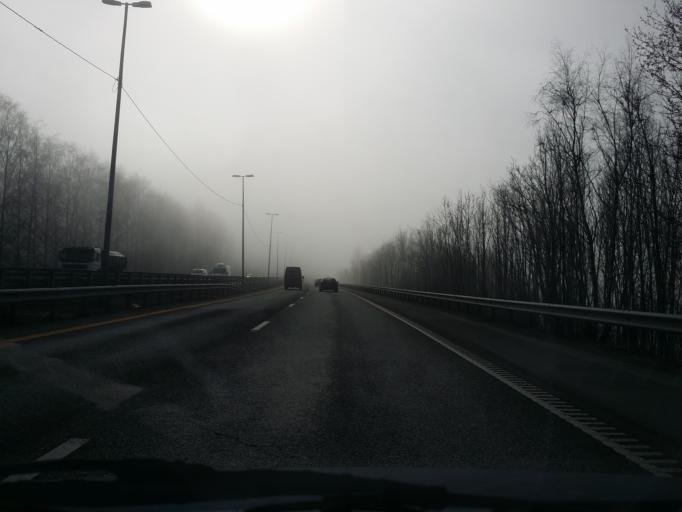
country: NO
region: Buskerud
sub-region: Lier
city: Tranby
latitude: 59.7823
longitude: 10.2741
